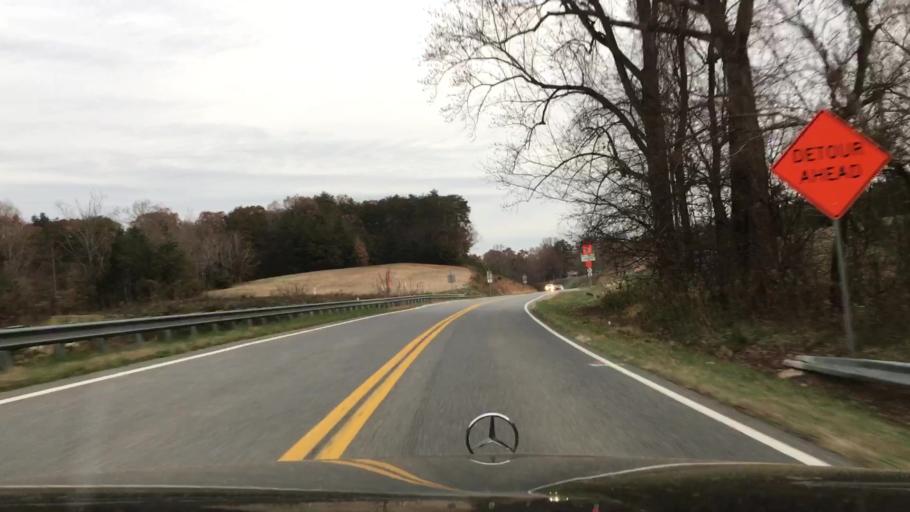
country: US
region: Virginia
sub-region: Campbell County
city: Altavista
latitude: 37.1799
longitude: -79.2938
